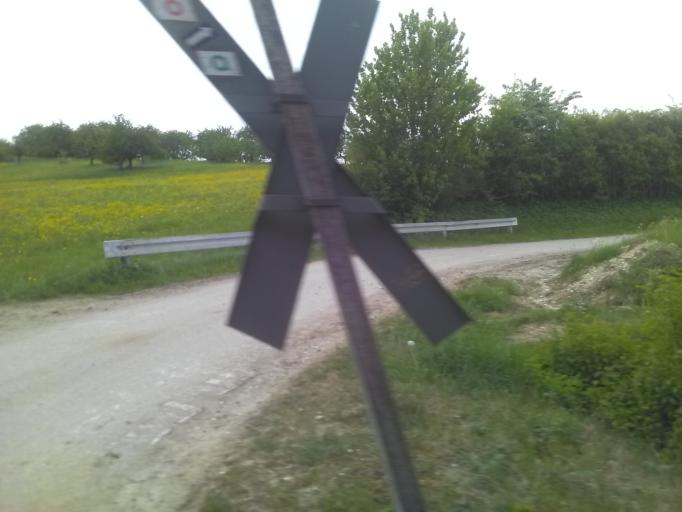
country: DE
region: Bavaria
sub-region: Regierungsbezirk Mittelfranken
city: Kalchreuth
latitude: 49.5612
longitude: 11.1516
